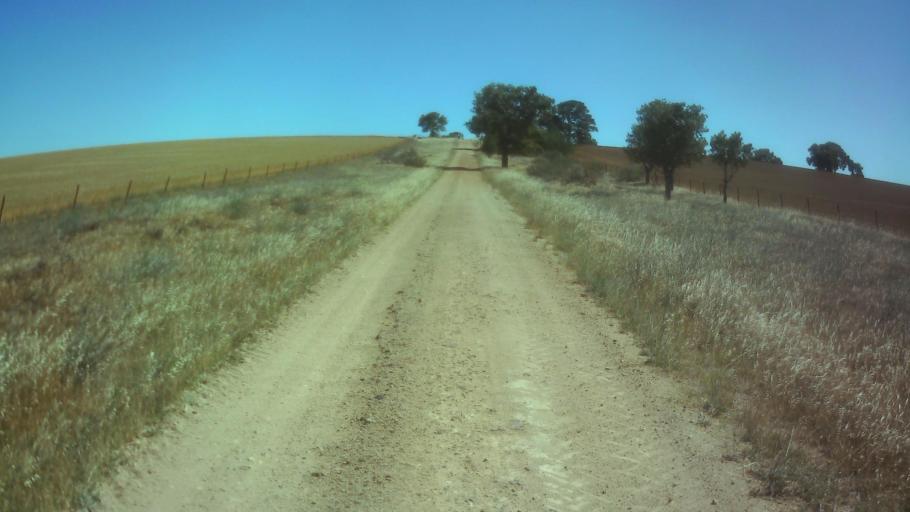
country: AU
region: New South Wales
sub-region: Weddin
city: Grenfell
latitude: -33.9718
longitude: 148.3435
